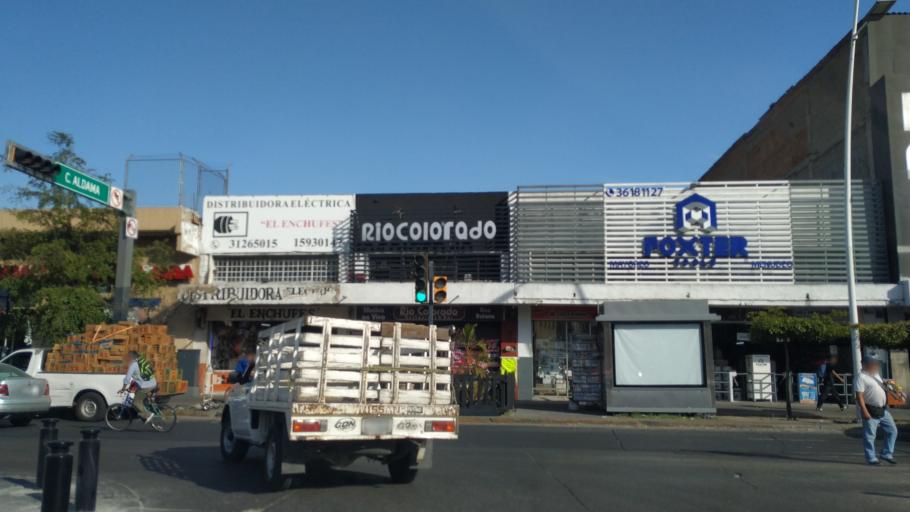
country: MX
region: Jalisco
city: Guadalajara
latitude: 20.6724
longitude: -103.3434
